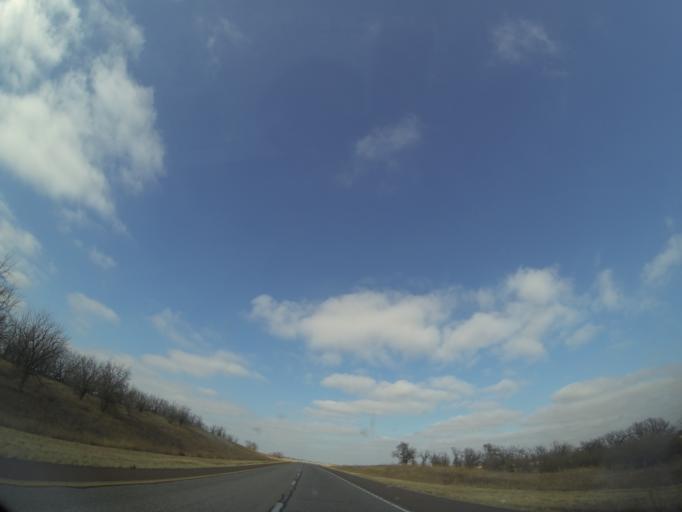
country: US
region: Kansas
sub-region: McPherson County
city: Lindsborg
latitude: 38.5155
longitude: -97.6196
